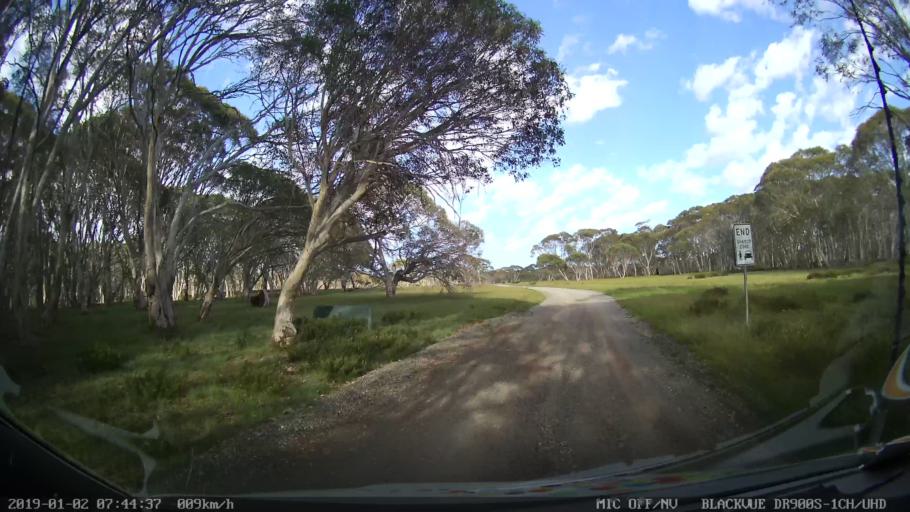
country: AU
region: New South Wales
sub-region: Tumut Shire
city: Tumut
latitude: -35.7763
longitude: 148.5174
